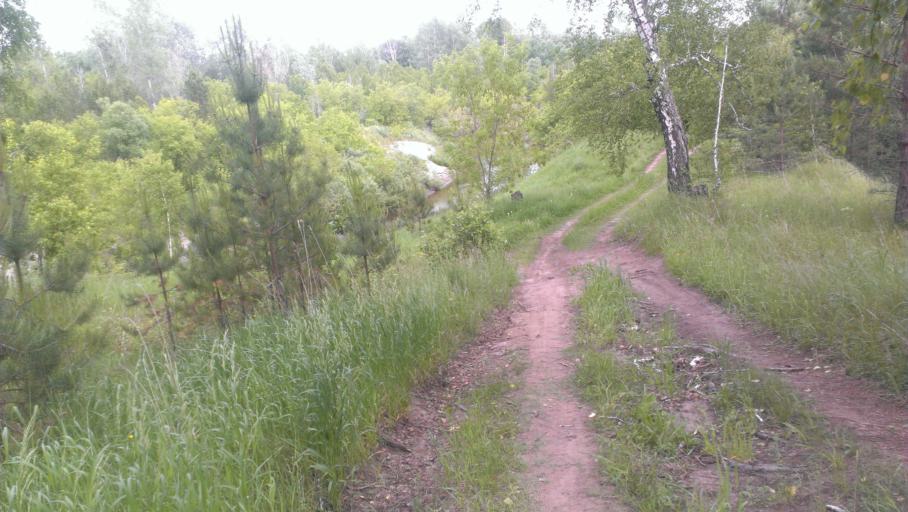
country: RU
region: Altai Krai
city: Sannikovo
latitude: 53.3394
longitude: 84.0576
